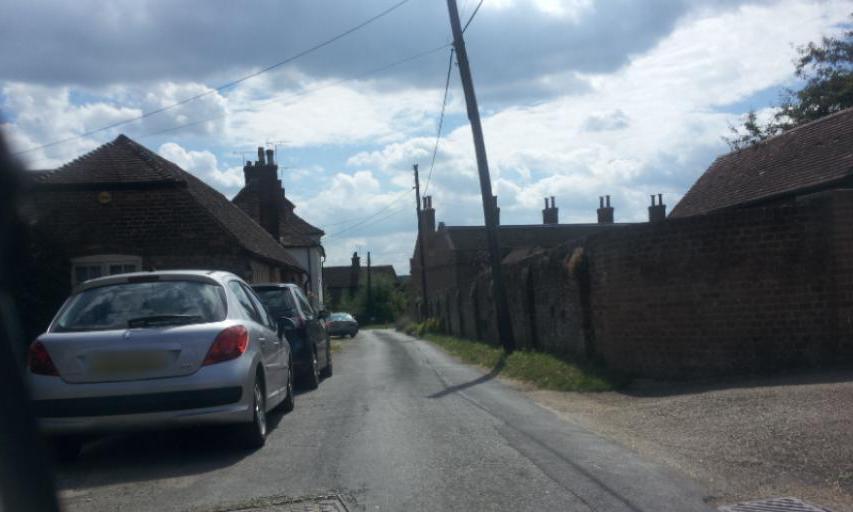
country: GB
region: England
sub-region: Kent
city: Harrietsham
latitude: 51.2405
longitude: 0.6810
